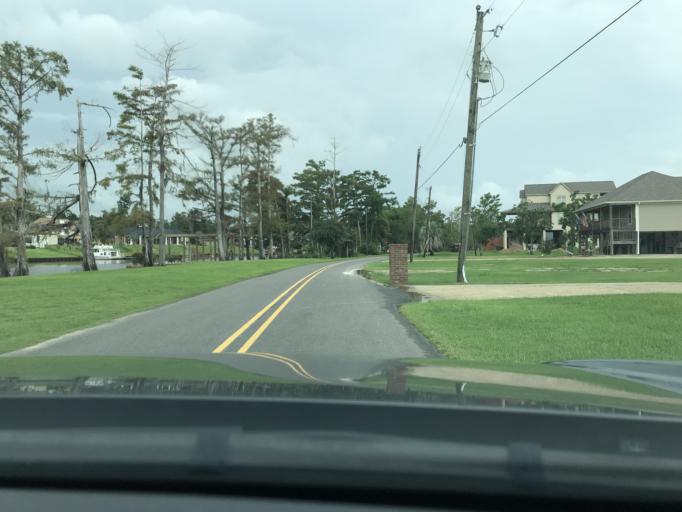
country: US
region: Louisiana
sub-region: Calcasieu Parish
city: Westlake
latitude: 30.2753
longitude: -93.2253
